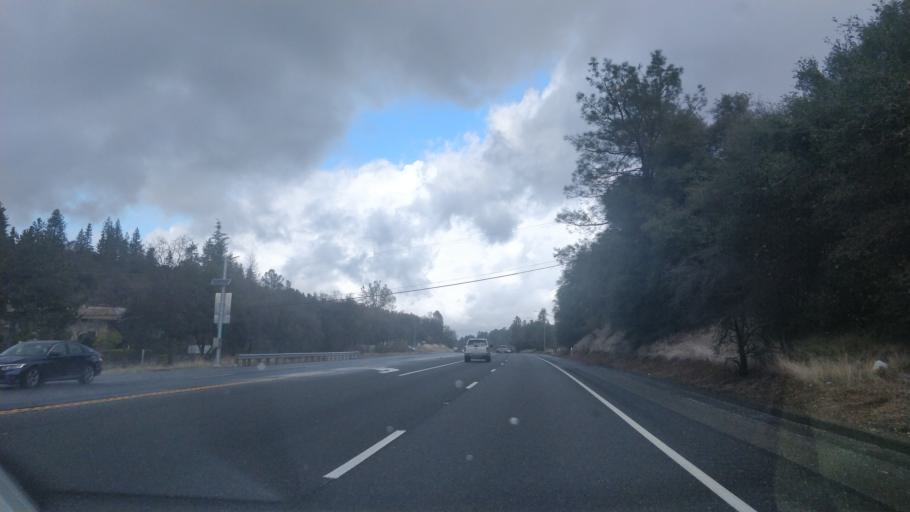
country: US
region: California
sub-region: Nevada County
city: Lake of the Pines
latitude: 39.0338
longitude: -121.0964
